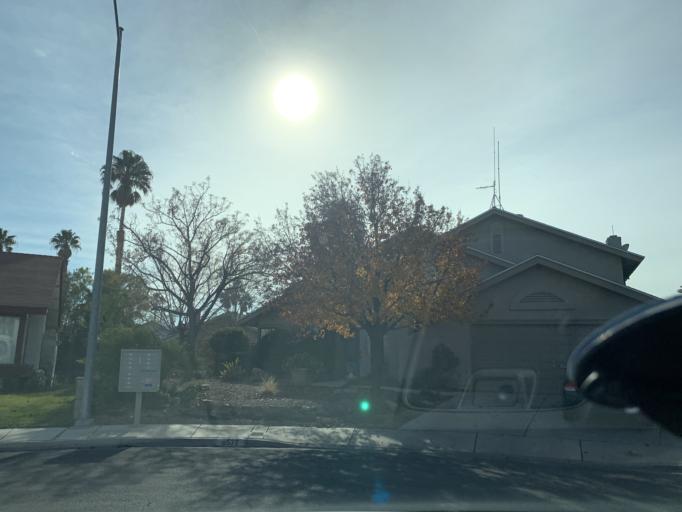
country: US
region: Nevada
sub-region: Clark County
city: Spring Valley
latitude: 36.1046
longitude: -115.2356
